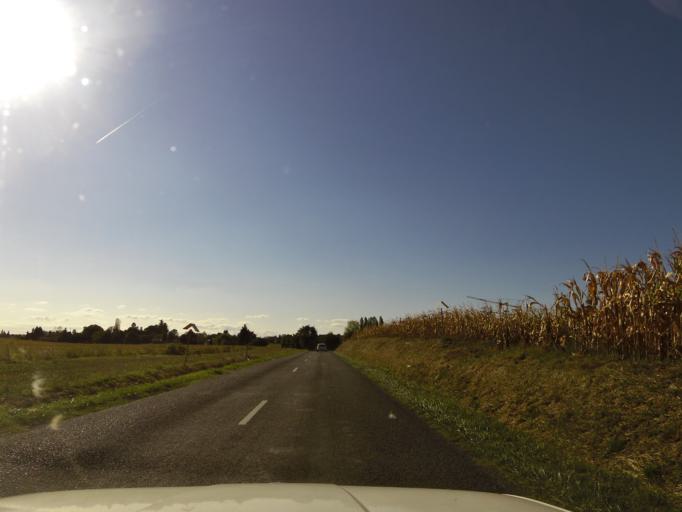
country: FR
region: Rhone-Alpes
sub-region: Departement de l'Ain
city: Chazey-sur-Ain
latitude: 45.8909
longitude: 5.2629
